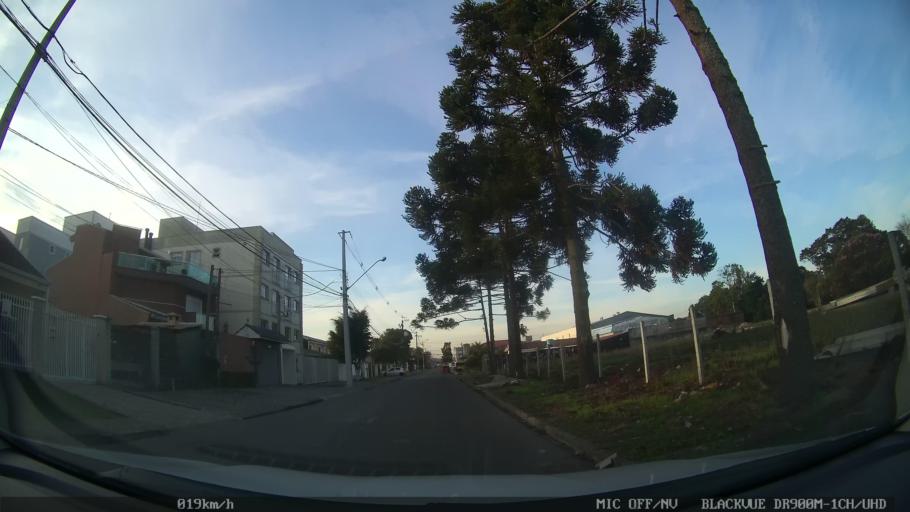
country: BR
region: Parana
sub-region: Pinhais
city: Pinhais
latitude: -25.4449
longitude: -49.1729
